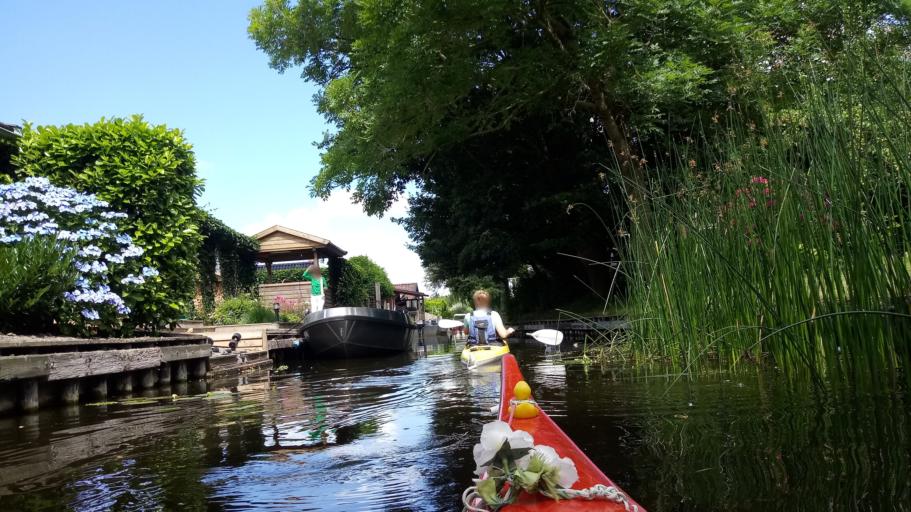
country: NL
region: Overijssel
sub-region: Gemeente Steenwijkerland
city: Wanneperveen
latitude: 52.7046
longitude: 6.1246
